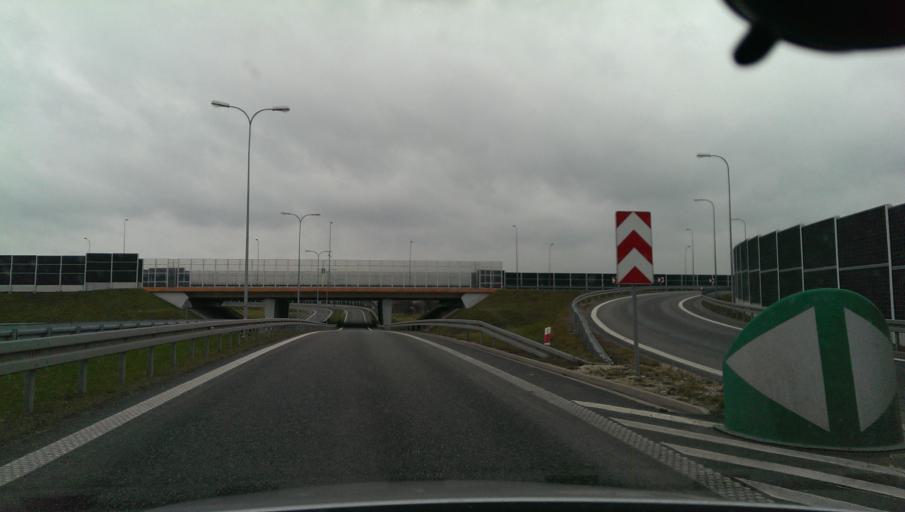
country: PL
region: Lesser Poland Voivodeship
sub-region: Powiat tarnowski
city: Wierzchoslawice
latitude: 50.0140
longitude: 20.8705
